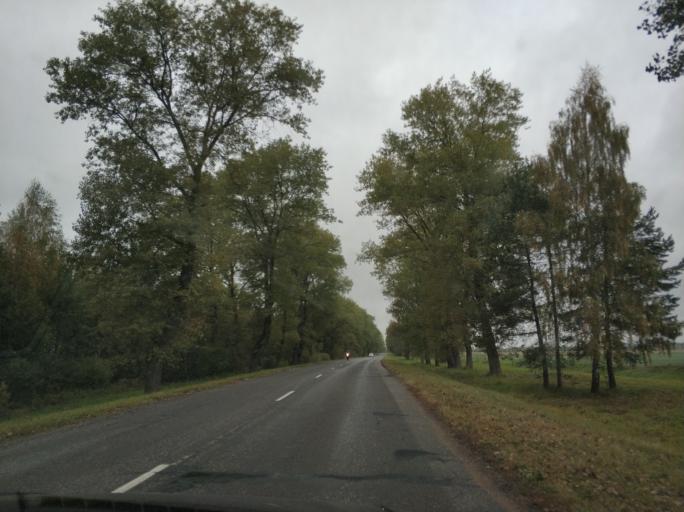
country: BY
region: Vitebsk
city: Polatsk
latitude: 55.4332
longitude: 28.9851
